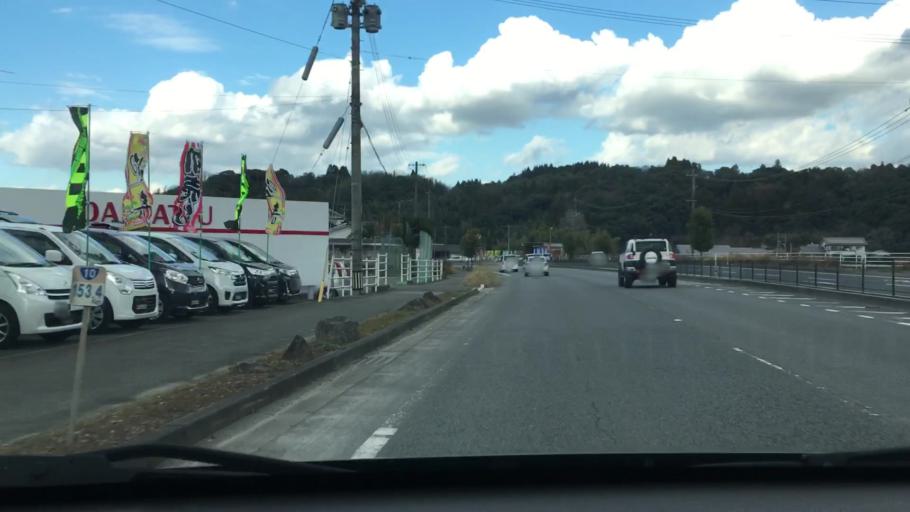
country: JP
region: Oita
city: Oita
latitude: 33.1320
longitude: 131.6594
